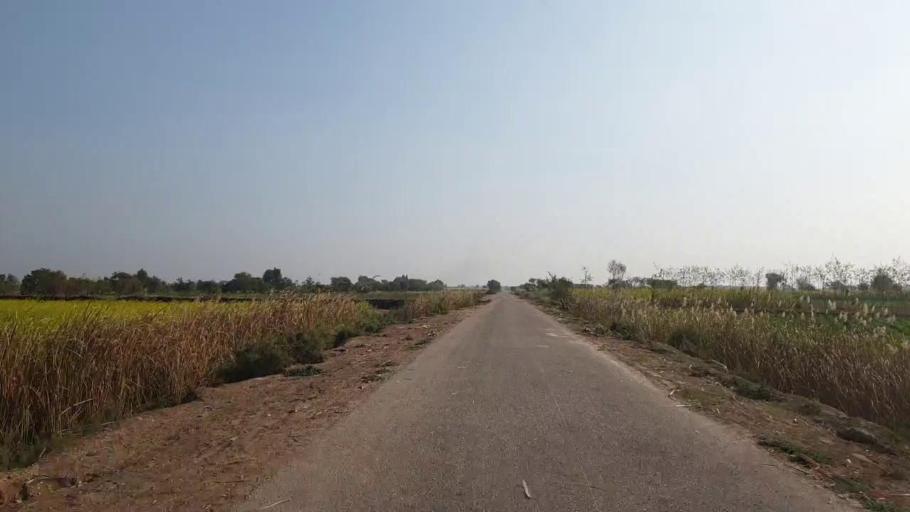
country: PK
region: Sindh
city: Tando Allahyar
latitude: 25.5902
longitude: 68.6206
